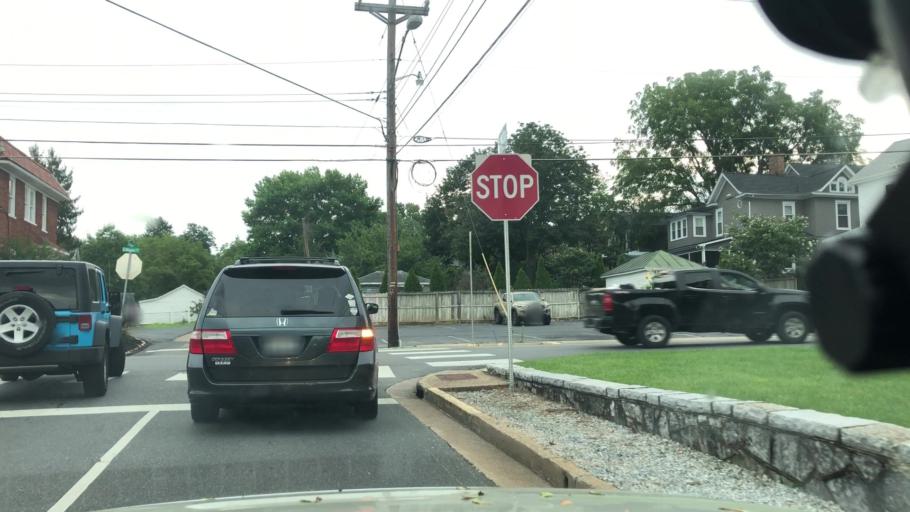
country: US
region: Virginia
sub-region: City of Harrisonburg
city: Harrisonburg
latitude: 38.4470
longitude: -78.8674
